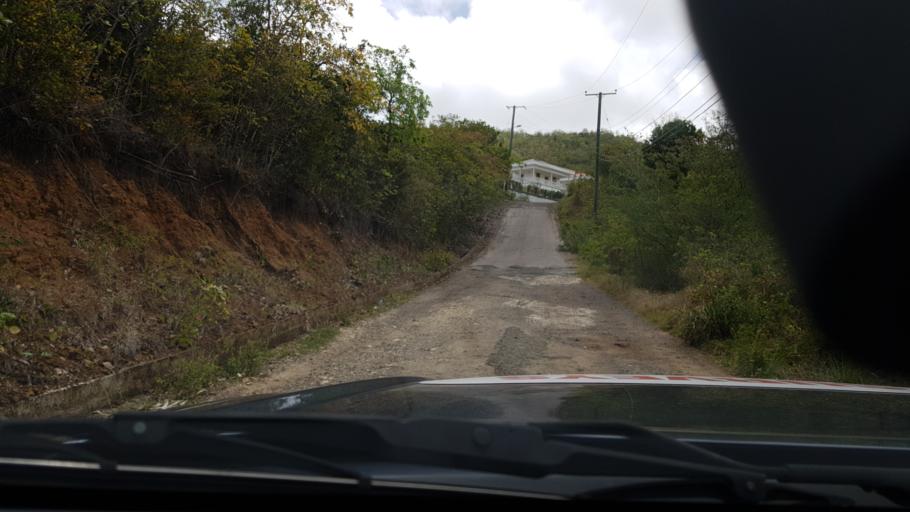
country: LC
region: Gros-Islet
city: Gros Islet
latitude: 14.0674
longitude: -60.9310
